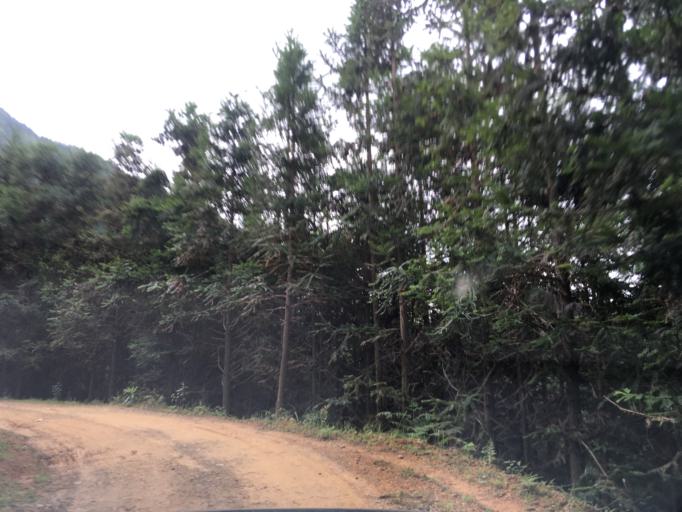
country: CN
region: Guangxi Zhuangzu Zizhiqu
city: Xinzhou
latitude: 24.8790
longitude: 105.8448
